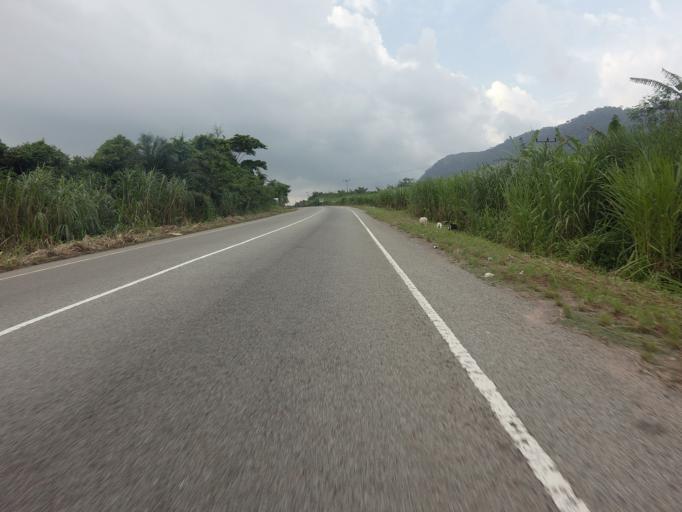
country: GH
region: Volta
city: Ho
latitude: 6.7620
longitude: 0.4797
